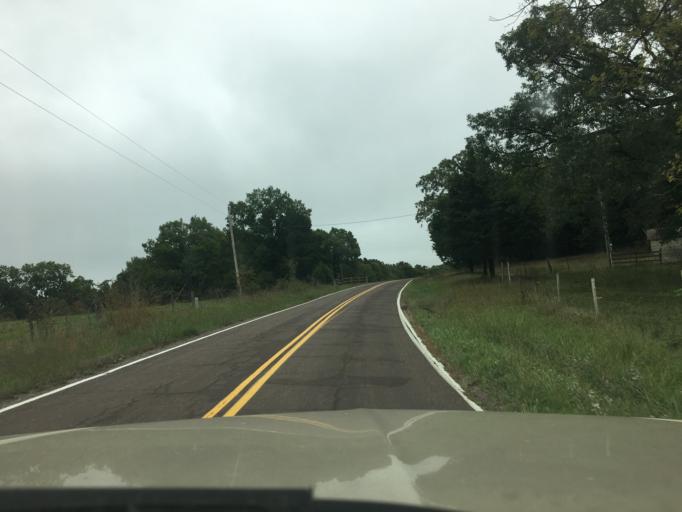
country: US
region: Missouri
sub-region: Crawford County
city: Cuba
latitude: 38.1934
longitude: -91.4668
